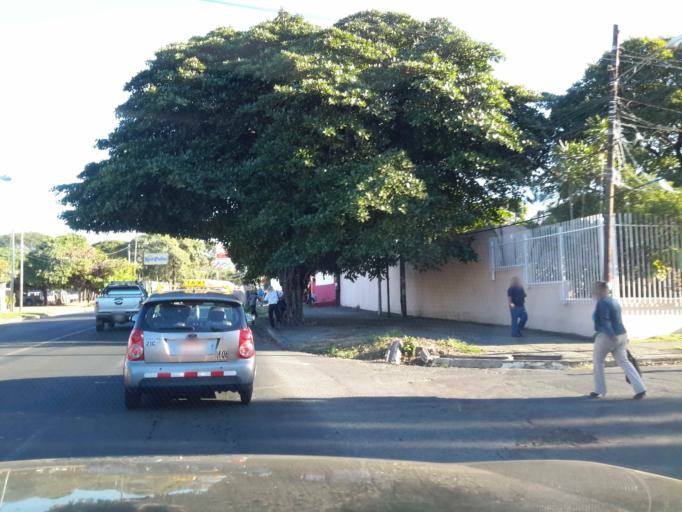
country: NI
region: Managua
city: Managua
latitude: 12.1374
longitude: -86.2822
